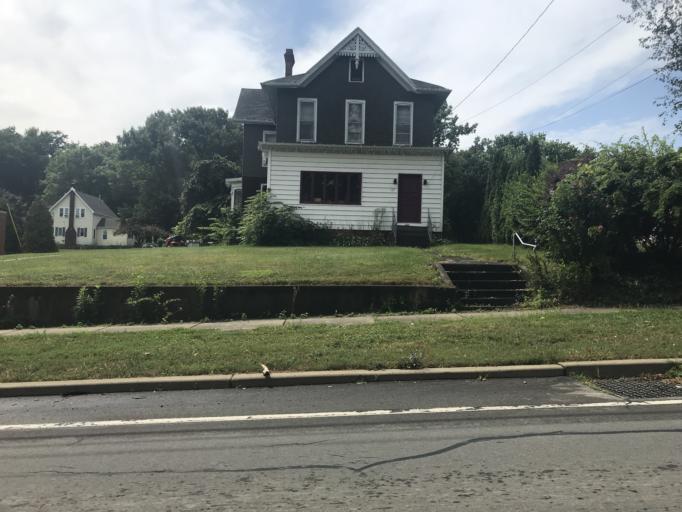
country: US
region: New York
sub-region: Chautauqua County
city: Silver Creek
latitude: 42.5457
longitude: -79.1734
